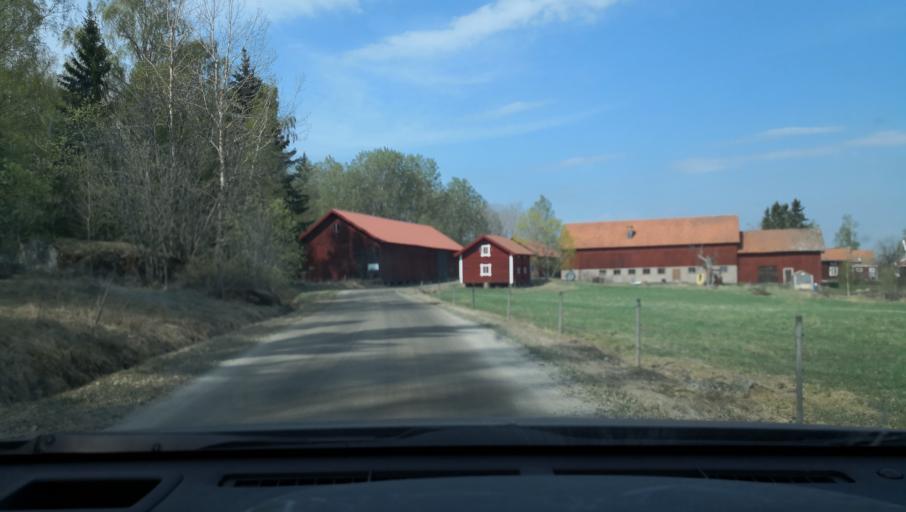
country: SE
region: Vaestmanland
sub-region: Vasteras
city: Skultuna
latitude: 59.7721
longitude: 16.4414
